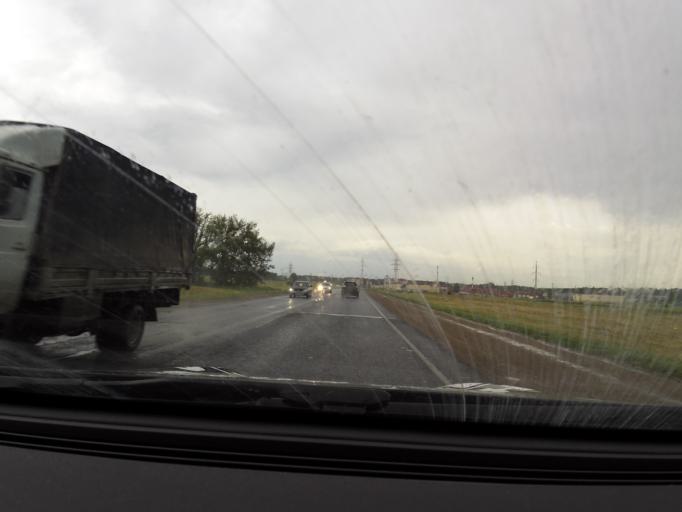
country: RU
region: Bashkortostan
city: Mikhaylovka
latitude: 54.8287
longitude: 55.8232
